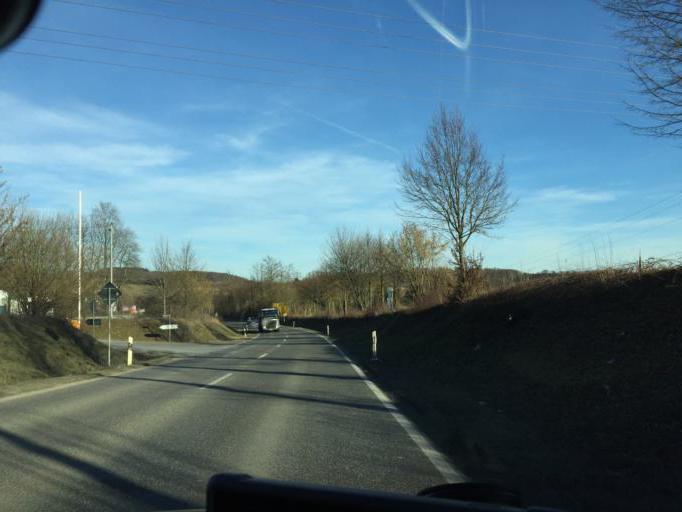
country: DE
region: Rheinland-Pfalz
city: Niederahr
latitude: 50.4753
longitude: 7.8554
